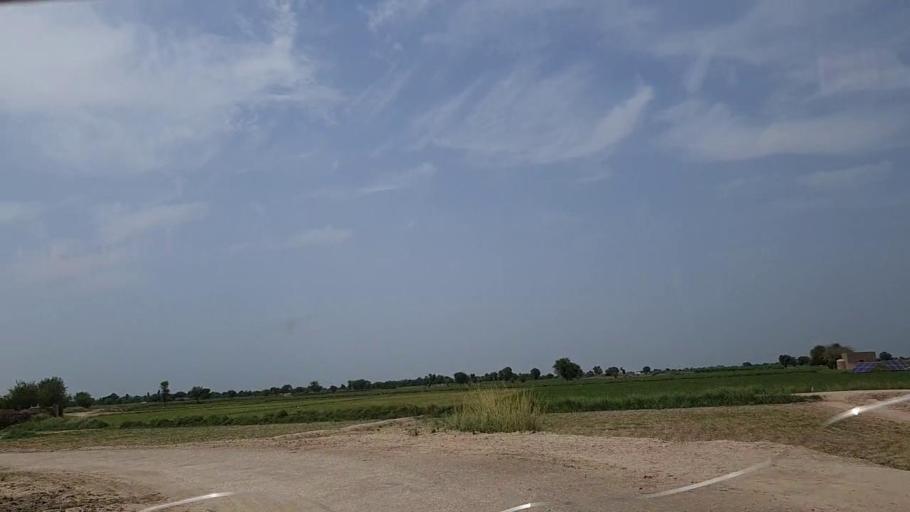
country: PK
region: Sindh
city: Tharu Shah
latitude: 26.8957
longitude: 68.0788
